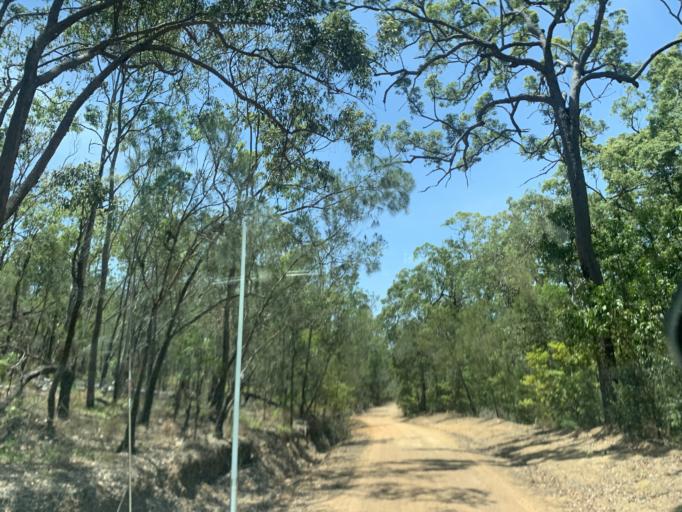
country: AU
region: Queensland
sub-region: Cairns
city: Redlynch
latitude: -16.9276
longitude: 145.6029
